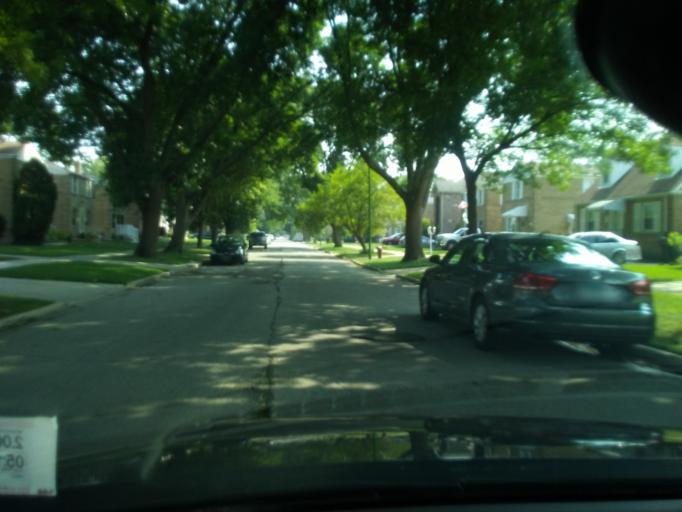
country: US
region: Illinois
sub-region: Cook County
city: Harwood Heights
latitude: 41.9749
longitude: -87.7916
